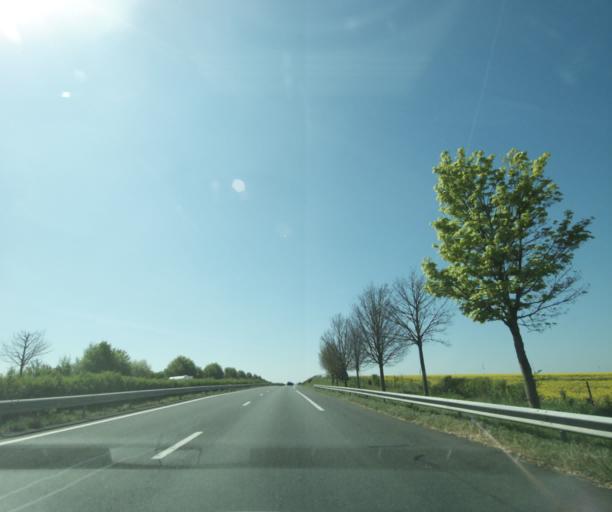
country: FR
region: Centre
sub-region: Departement de l'Indre
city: Vatan
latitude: 47.0311
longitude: 1.7906
